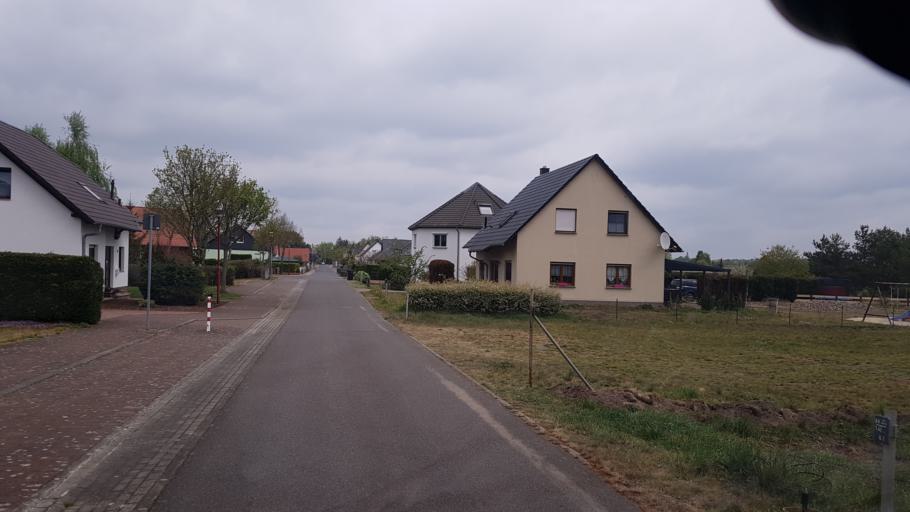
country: DE
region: Brandenburg
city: Altdobern
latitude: 51.6435
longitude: 14.0226
